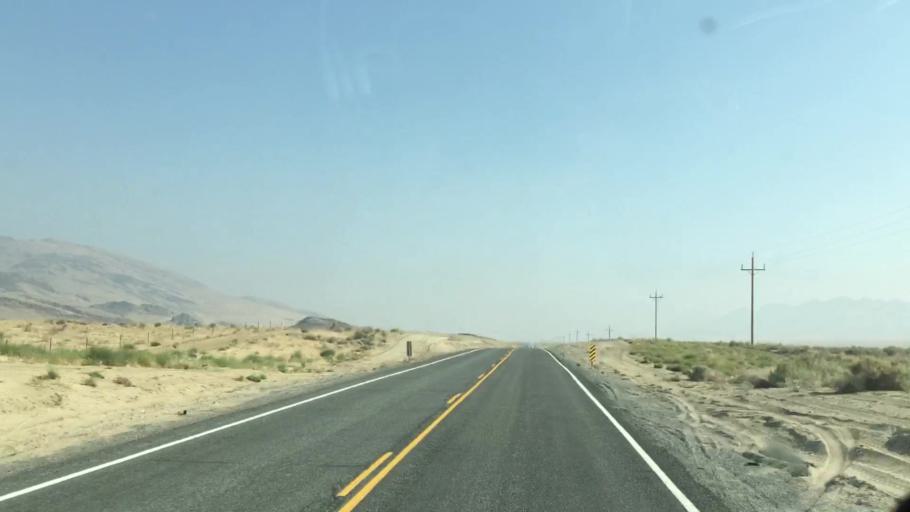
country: US
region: Nevada
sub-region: Lyon County
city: Fernley
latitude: 40.3578
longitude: -119.3376
